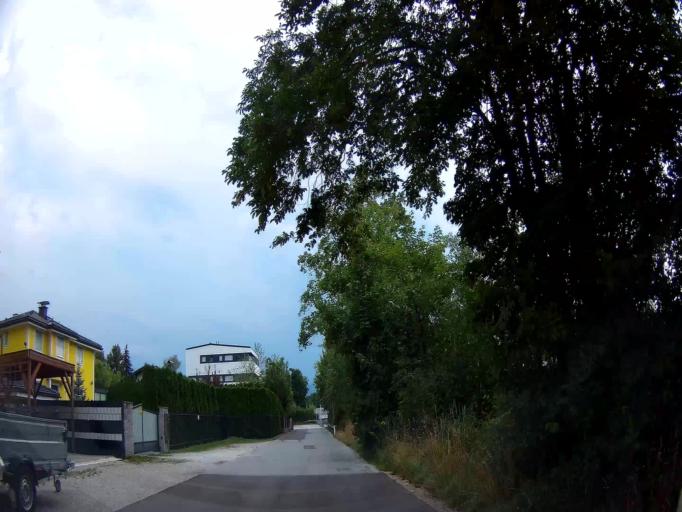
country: DE
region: Bavaria
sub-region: Upper Bavaria
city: Freilassing
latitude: 47.8361
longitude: 12.9966
